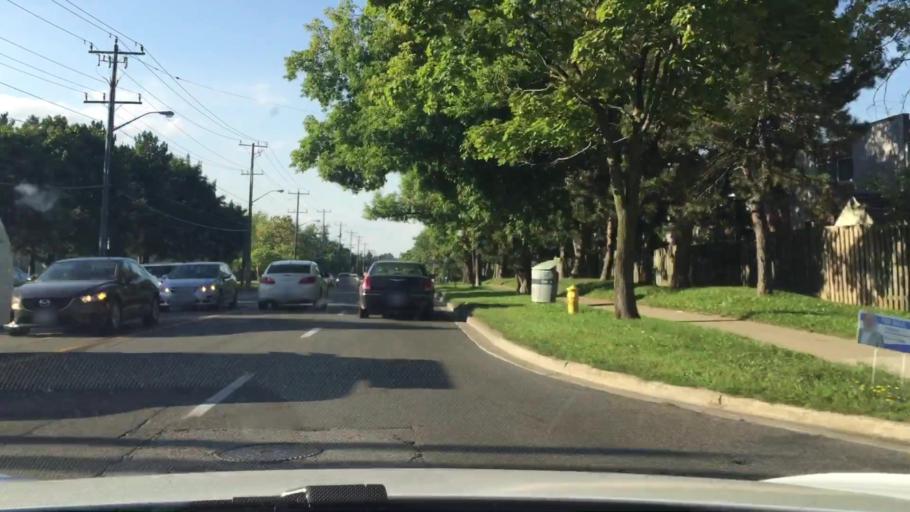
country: CA
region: Ontario
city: Scarborough
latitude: 43.7837
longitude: -79.2994
